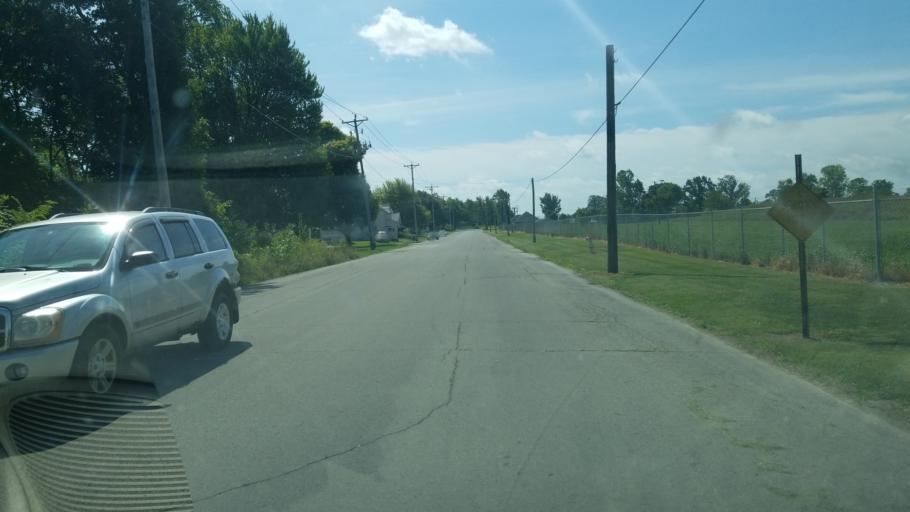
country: US
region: Ohio
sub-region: Hardin County
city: Kenton
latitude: 40.6366
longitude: -83.6084
